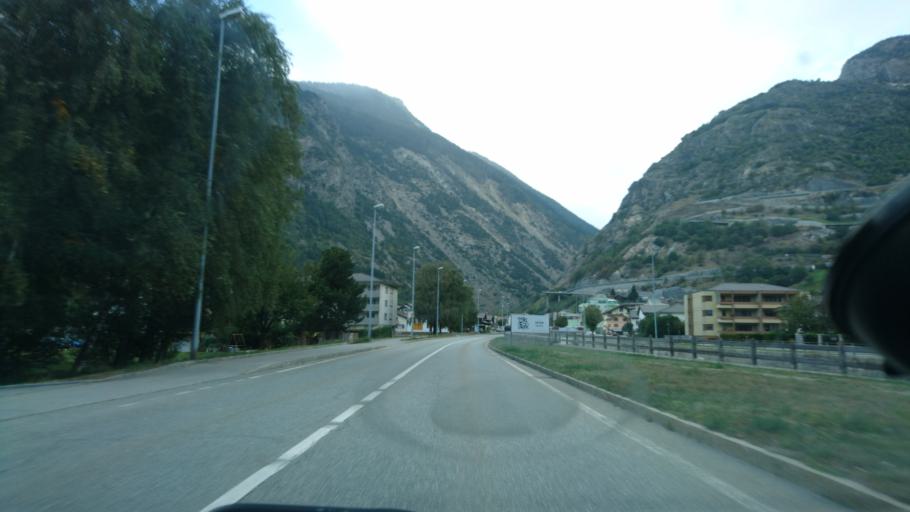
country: CH
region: Valais
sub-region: Leuk District
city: Gampel
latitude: 46.3123
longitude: 7.7448
